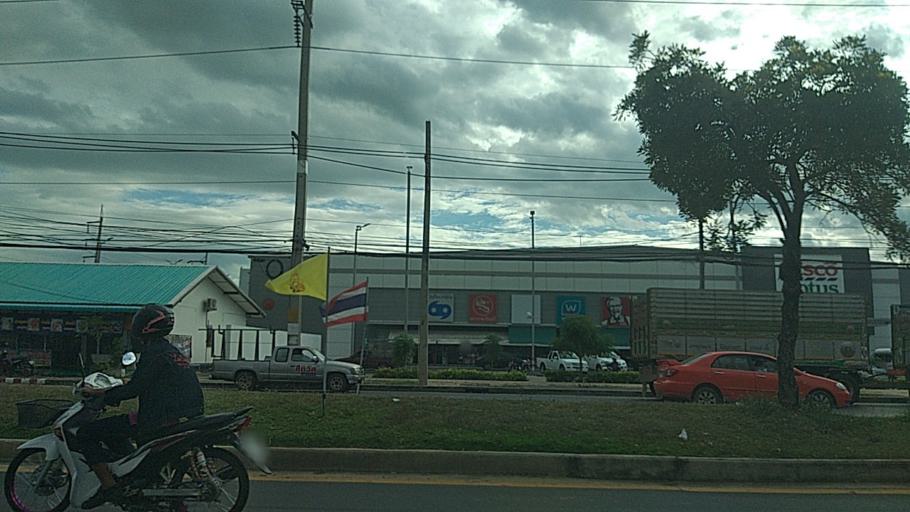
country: TH
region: Surin
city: Prasat
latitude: 14.6314
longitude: 103.4083
